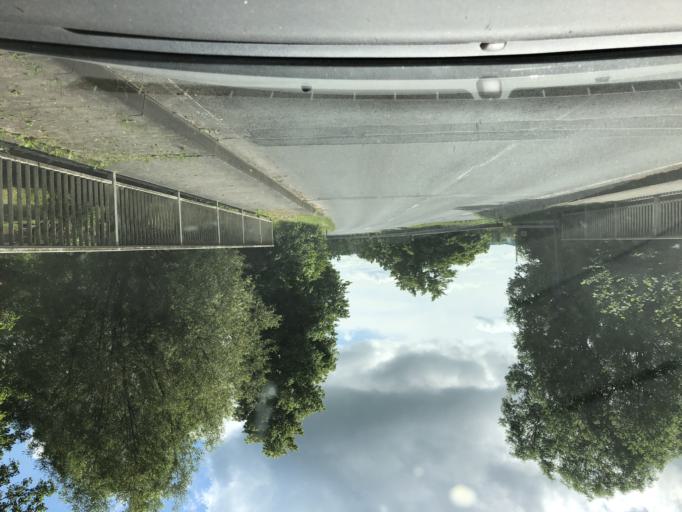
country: DE
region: Hesse
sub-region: Regierungsbezirk Kassel
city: Alheim
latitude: 51.0641
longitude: 9.6086
